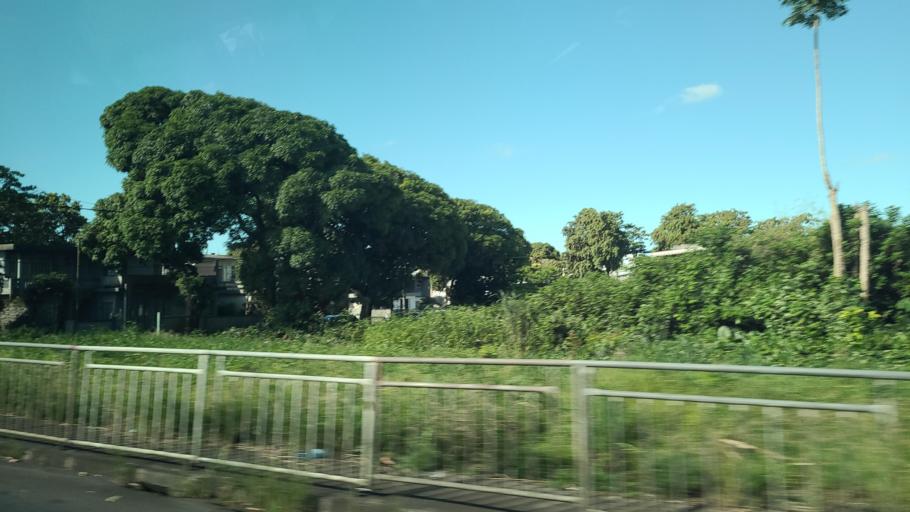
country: MU
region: Flacq
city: Lalmatie
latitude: -20.2058
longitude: 57.6750
